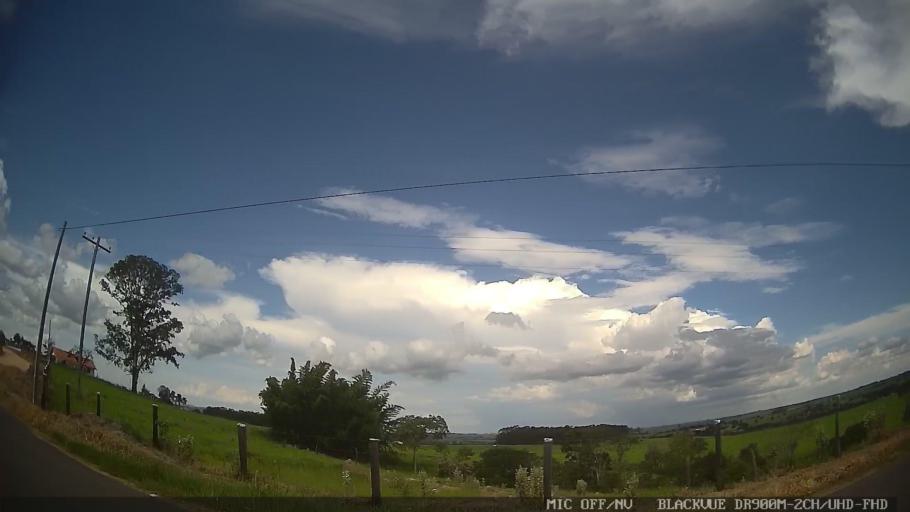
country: BR
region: Sao Paulo
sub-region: Conchas
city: Conchas
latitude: -22.9500
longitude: -47.9826
